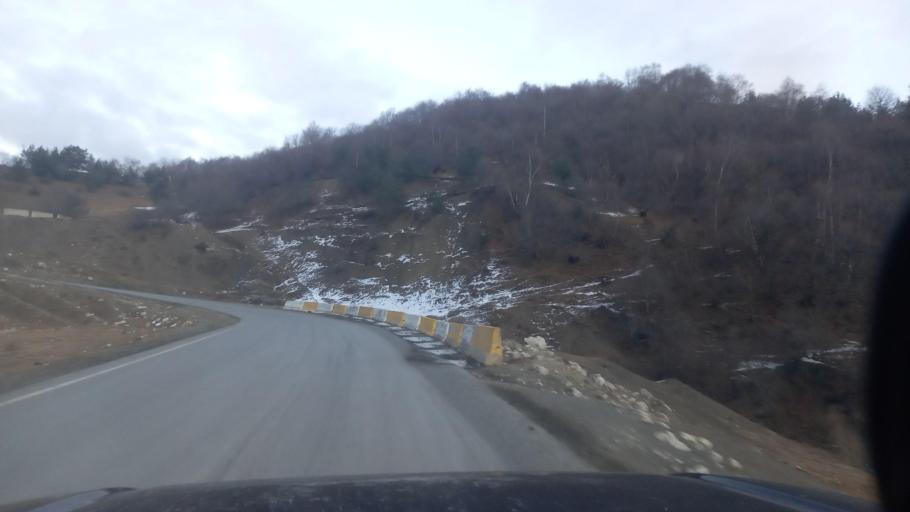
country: RU
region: Ingushetiya
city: Dzhayrakh
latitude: 42.8208
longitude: 44.8166
